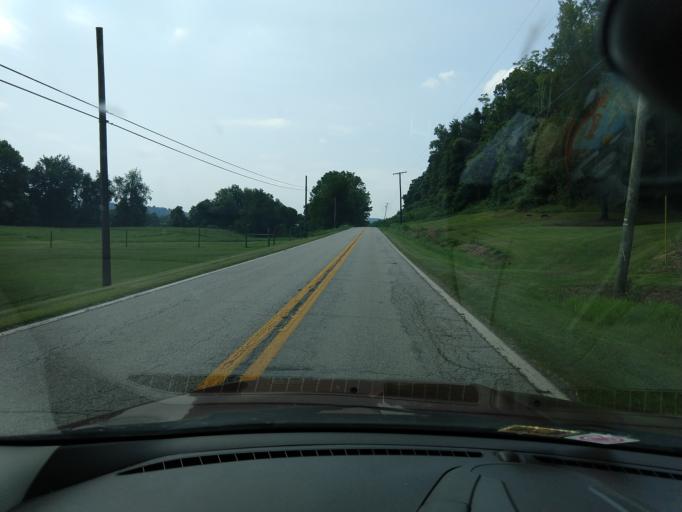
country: US
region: West Virginia
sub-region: Mason County
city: New Haven
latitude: 38.9295
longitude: -81.9141
